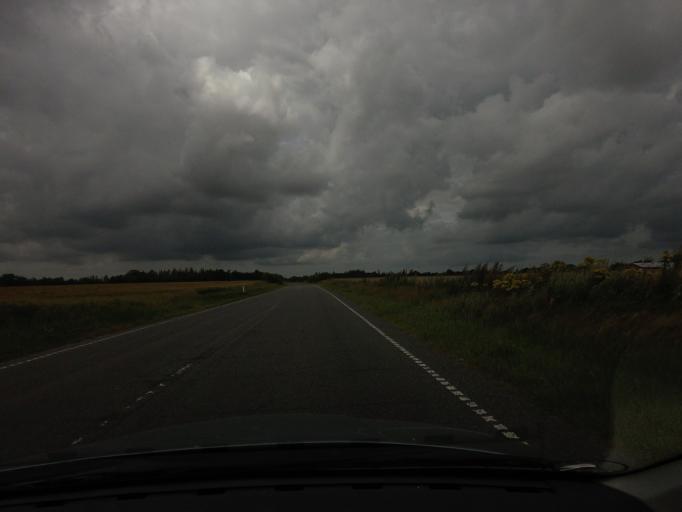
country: DK
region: North Denmark
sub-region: Hjorring Kommune
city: Hjorring
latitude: 57.4235
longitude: 10.0036
